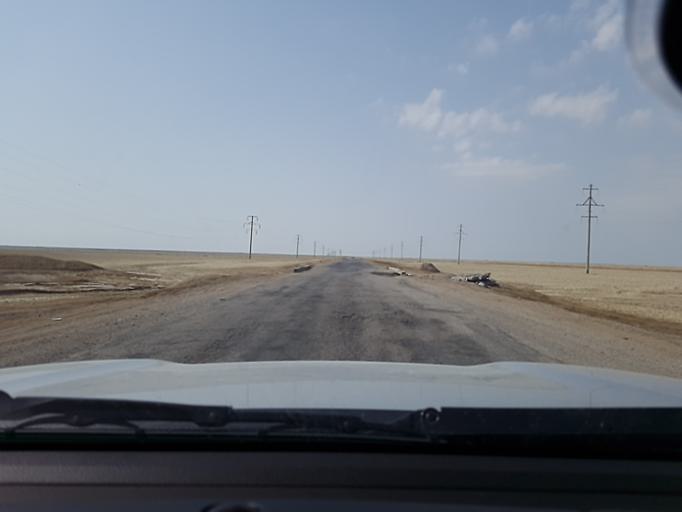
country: TM
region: Balkan
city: Gumdag
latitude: 39.0665
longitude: 54.5842
